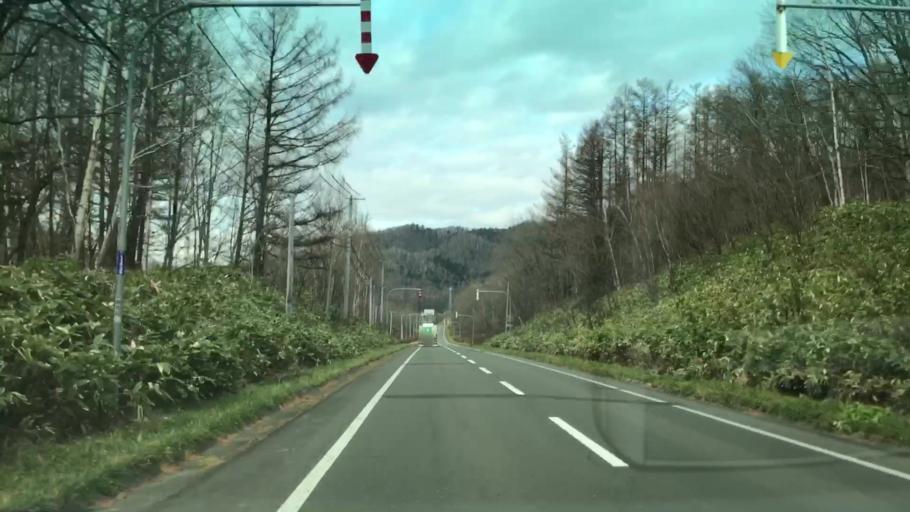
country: JP
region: Hokkaido
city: Shimo-furano
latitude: 42.9416
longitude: 142.4443
